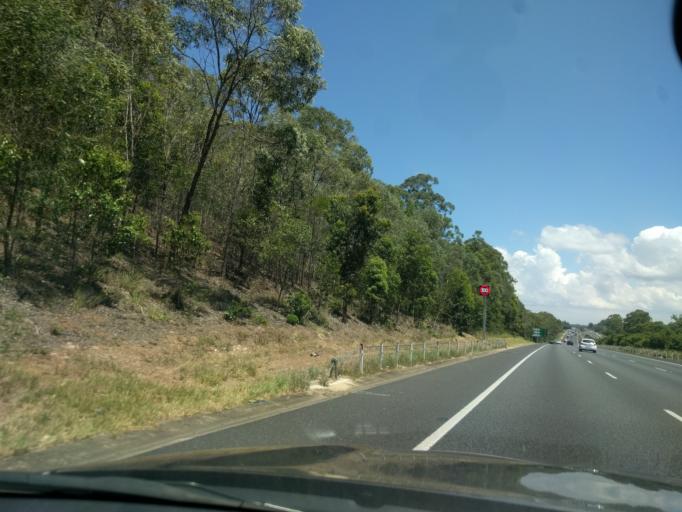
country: AU
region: Queensland
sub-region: Moreton Bay
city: Narangba
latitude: -27.1873
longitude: 152.9863
